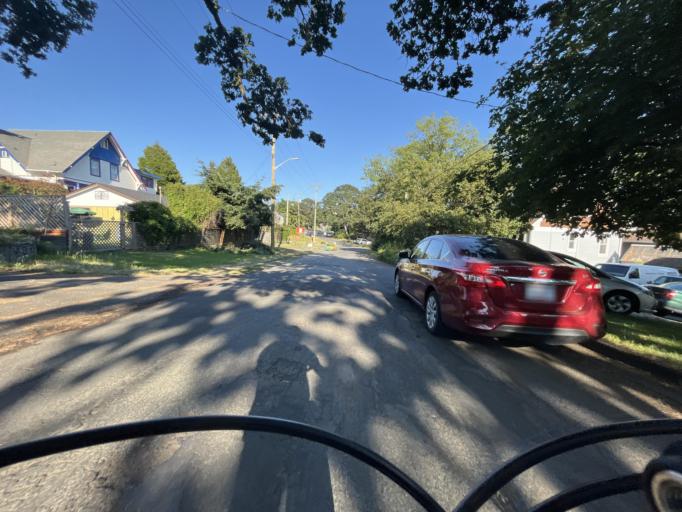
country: CA
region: British Columbia
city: Victoria
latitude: 48.4383
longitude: -123.3467
